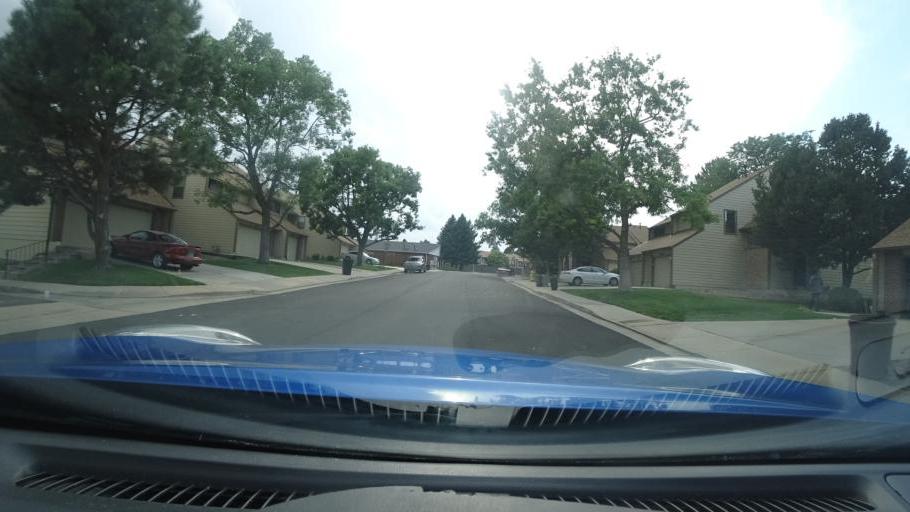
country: US
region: Colorado
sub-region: Adams County
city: Aurora
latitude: 39.6928
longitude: -104.8084
